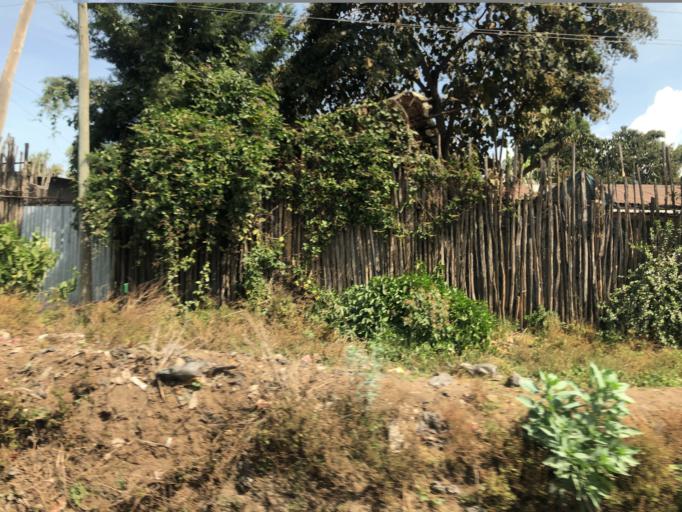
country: ET
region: Oromiya
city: Shashemene
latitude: 7.2705
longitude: 38.6558
